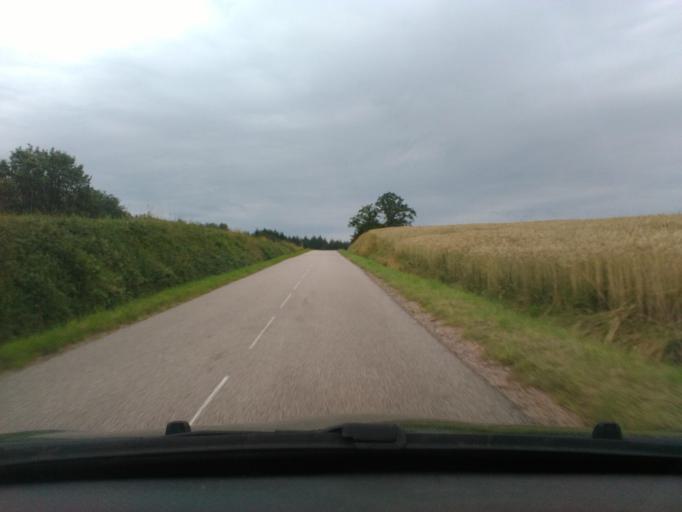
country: FR
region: Lorraine
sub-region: Departement des Vosges
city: Bruyeres
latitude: 48.2164
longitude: 6.7545
